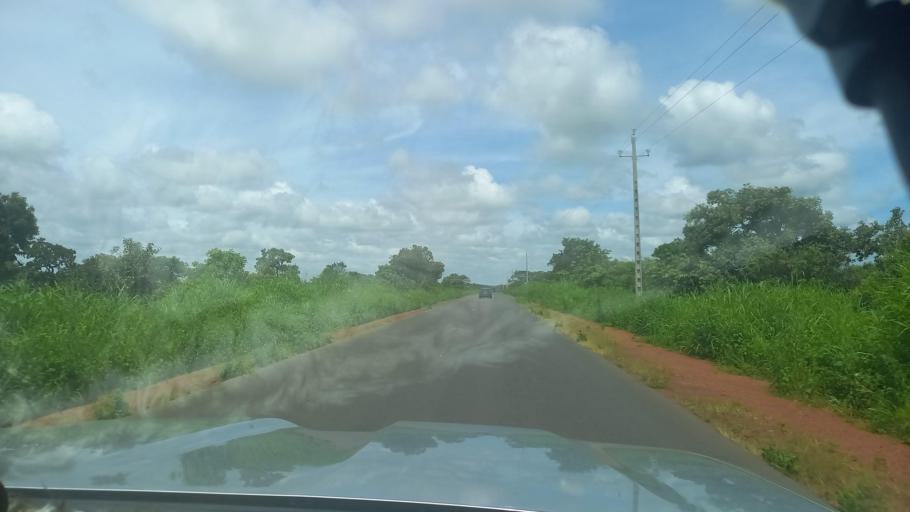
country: GM
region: Lower River
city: Kaiaf
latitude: 13.1917
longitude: -15.5557
